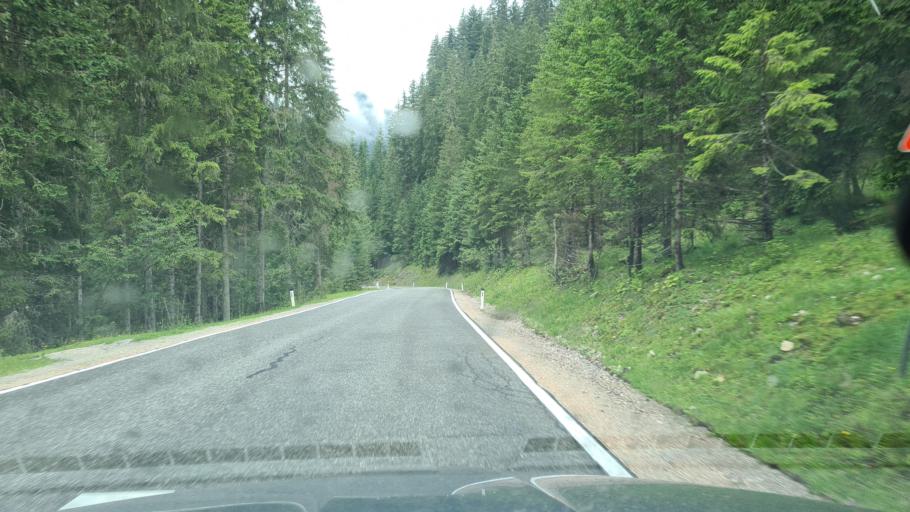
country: AT
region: Salzburg
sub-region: Politischer Bezirk Sankt Johann im Pongau
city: Untertauern
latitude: 47.3061
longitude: 13.4519
